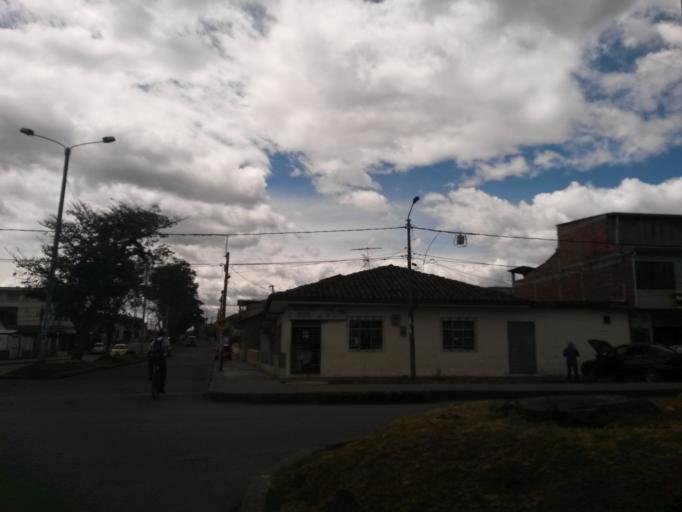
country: CO
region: Cauca
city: Popayan
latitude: 2.4356
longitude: -76.6123
